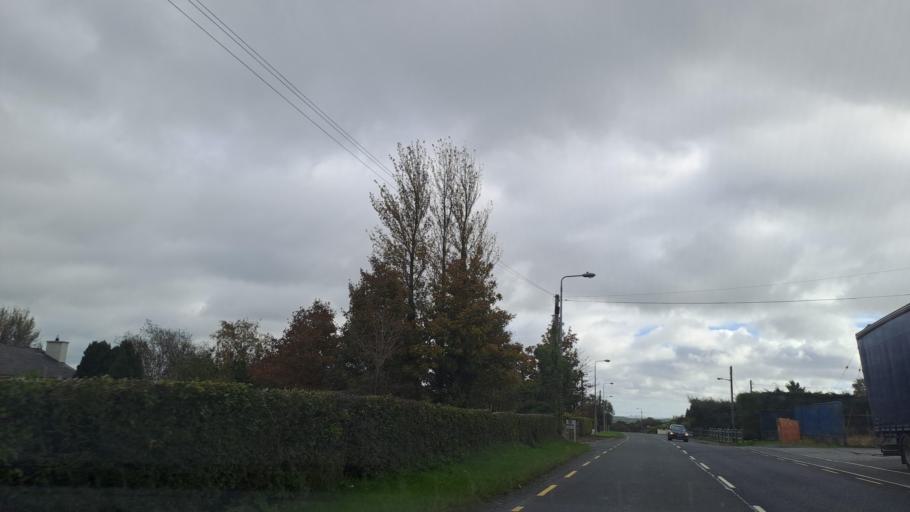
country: IE
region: Ulster
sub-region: An Cabhan
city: Kingscourt
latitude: 53.9096
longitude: -6.8139
